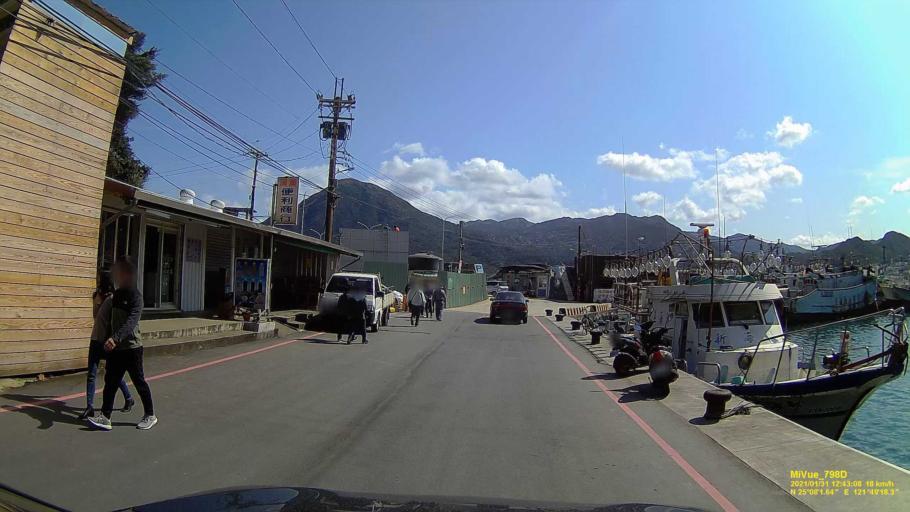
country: TW
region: Taiwan
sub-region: Keelung
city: Keelung
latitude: 25.1337
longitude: 121.8219
